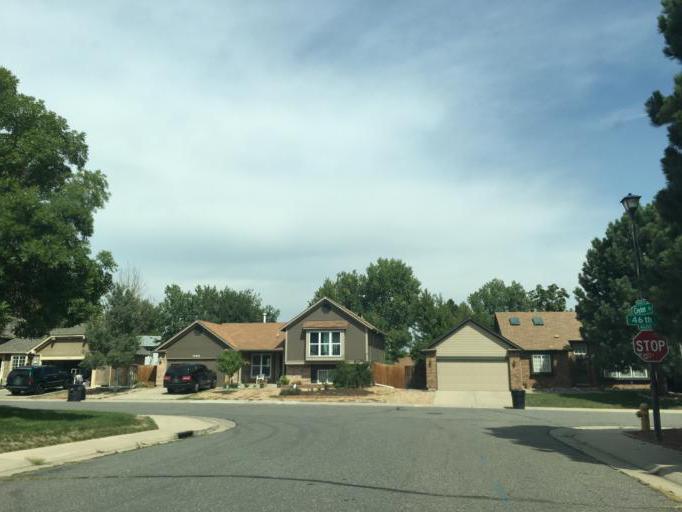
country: US
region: Colorado
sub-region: Adams County
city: Aurora
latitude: 39.7798
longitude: -104.7634
